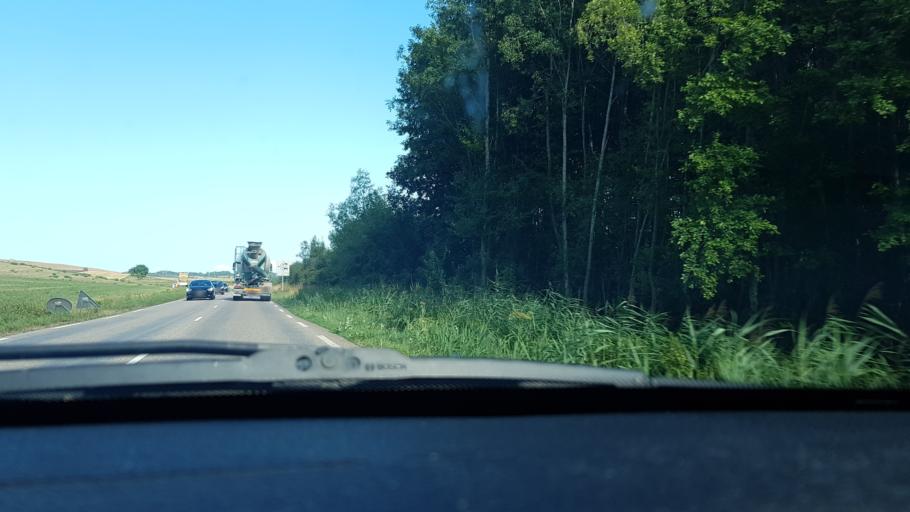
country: FR
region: Lorraine
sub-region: Departement des Vosges
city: Charmes
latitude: 48.3615
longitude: 6.2286
